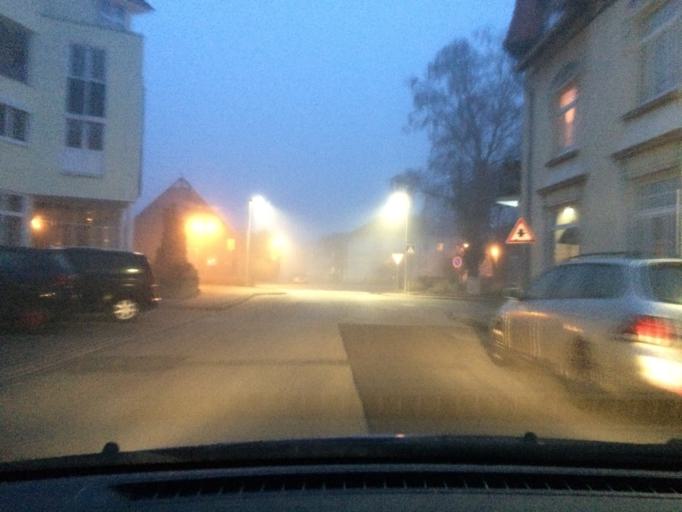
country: DE
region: Schleswig-Holstein
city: Geesthacht
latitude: 53.4321
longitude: 10.3750
